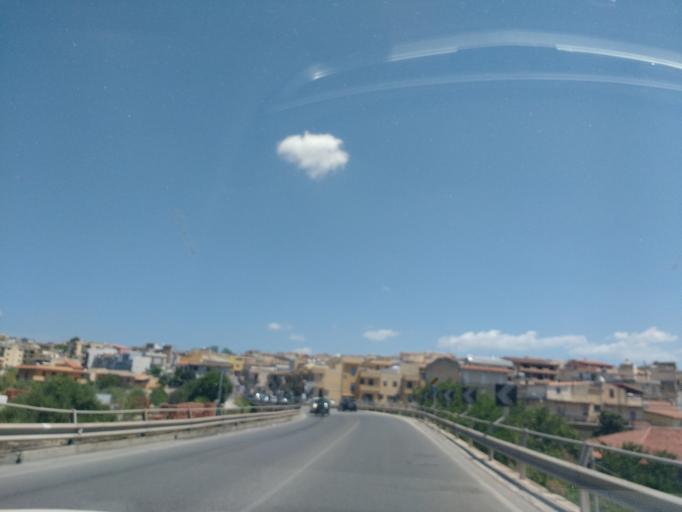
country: IT
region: Sicily
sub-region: Provincia di Siracusa
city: Noto
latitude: 36.8873
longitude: 15.0620
